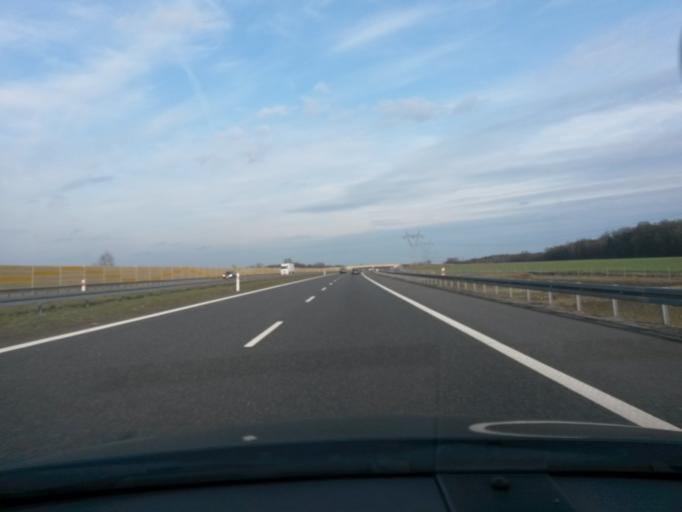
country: PL
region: Lodz Voivodeship
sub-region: Powiat zgierski
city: Ozorkow
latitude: 51.9280
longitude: 19.3115
